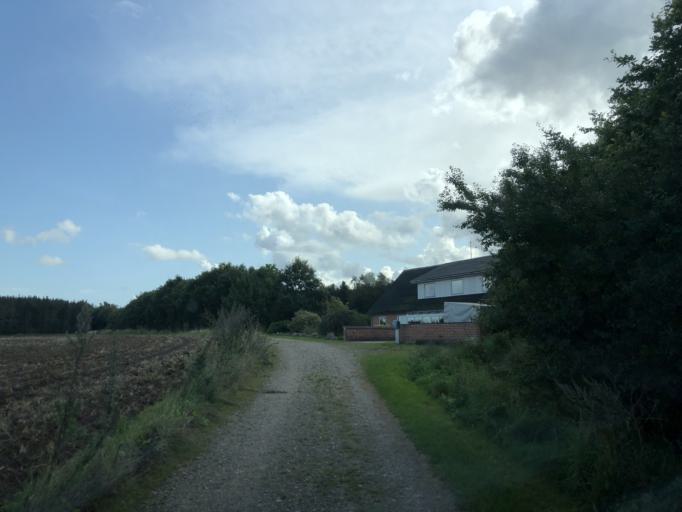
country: DK
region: Central Jutland
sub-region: Favrskov Kommune
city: Hadsten
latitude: 56.3209
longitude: 10.0183
